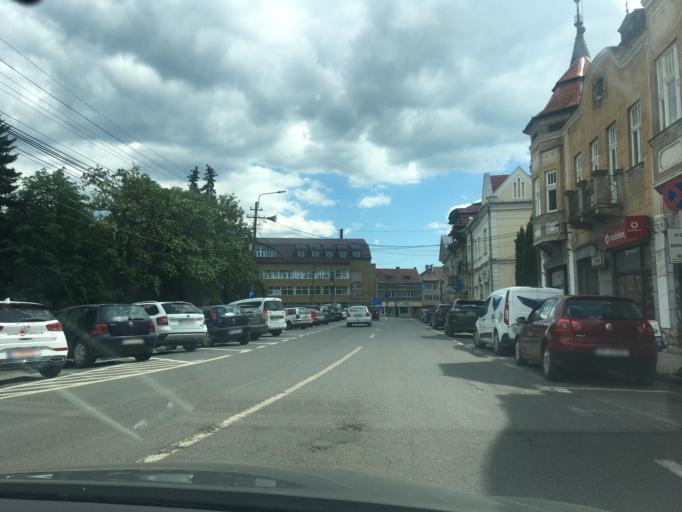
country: RO
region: Harghita
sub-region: Municipiul Gheorgheni
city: Gheorgheni
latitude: 46.7217
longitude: 25.5989
